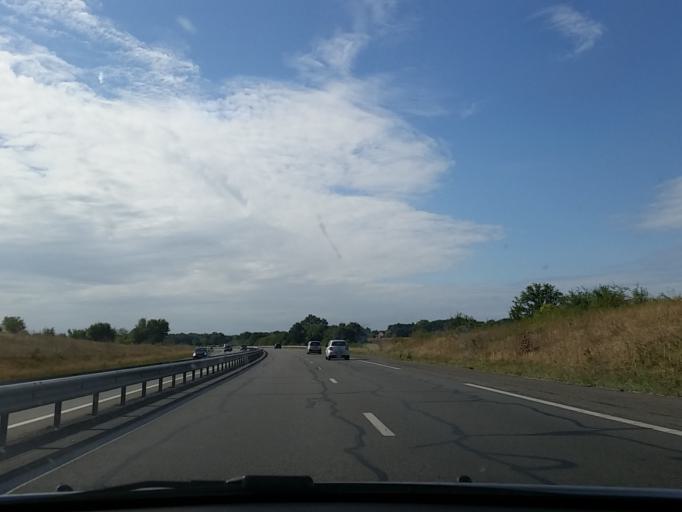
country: FR
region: Centre
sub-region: Departement du Cher
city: Orval
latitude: 46.7726
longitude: 2.4058
